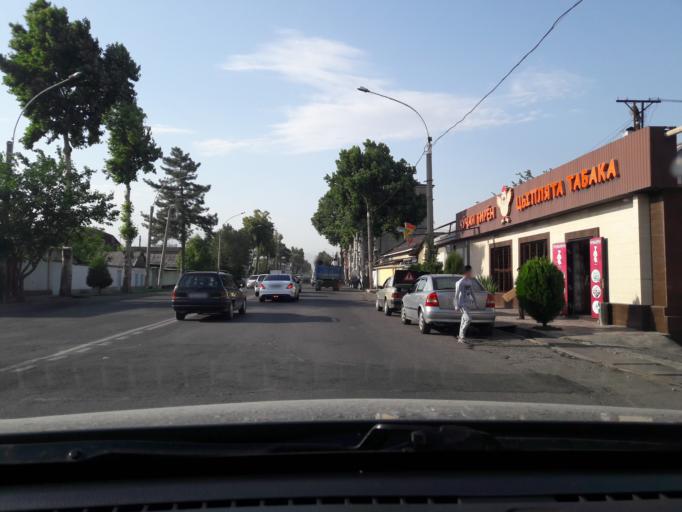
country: TJ
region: Dushanbe
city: Dushanbe
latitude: 38.5488
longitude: 68.7720
